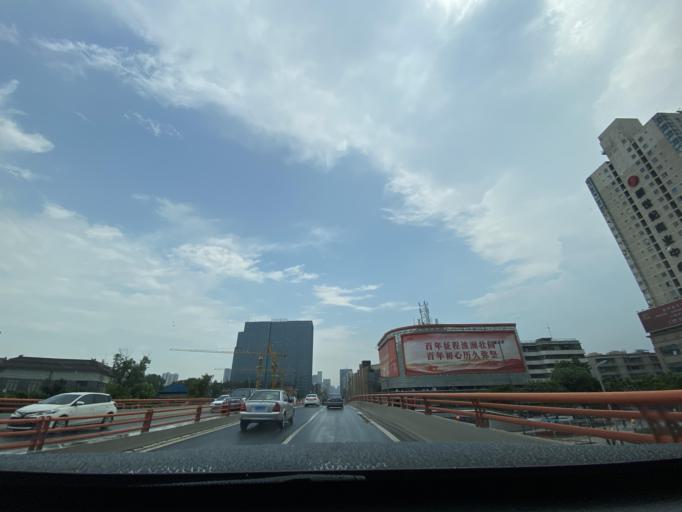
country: CN
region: Sichuan
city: Chengdu
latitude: 30.6364
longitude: 104.0736
